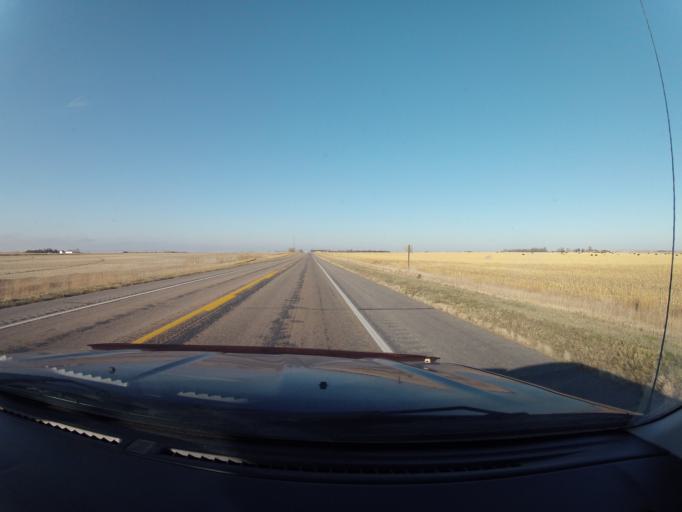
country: US
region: Nebraska
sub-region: Kearney County
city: Minden
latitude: 40.5616
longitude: -98.9518
